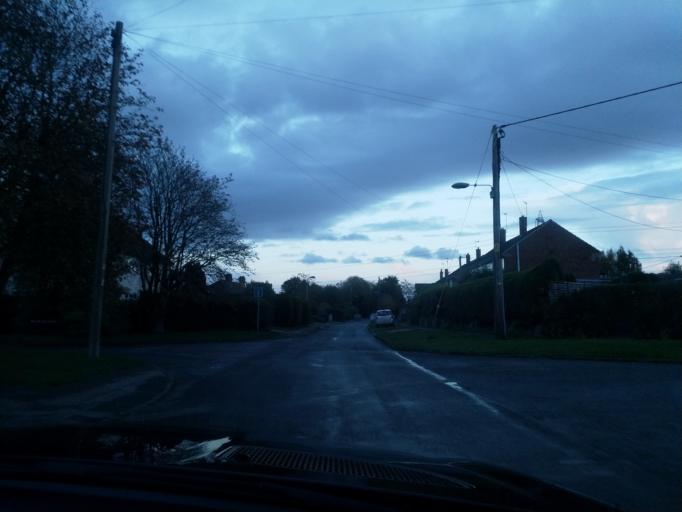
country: GB
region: England
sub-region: Oxfordshire
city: Wheatley
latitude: 51.7437
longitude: -1.1278
